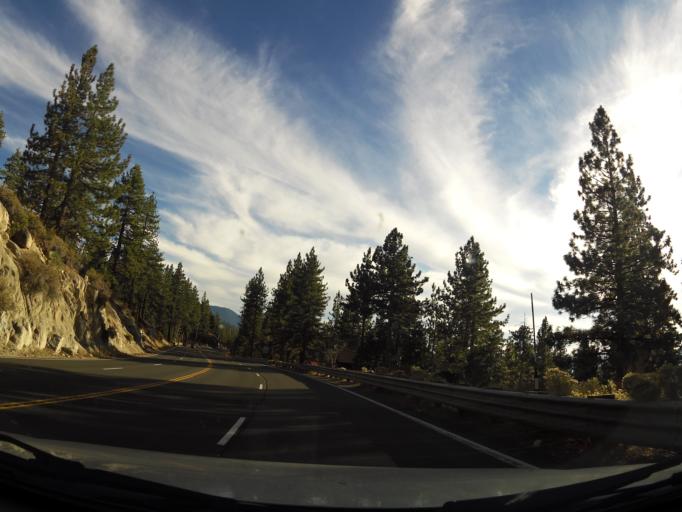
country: US
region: Nevada
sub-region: Douglas County
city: Kingsbury
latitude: 39.0319
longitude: -119.9471
